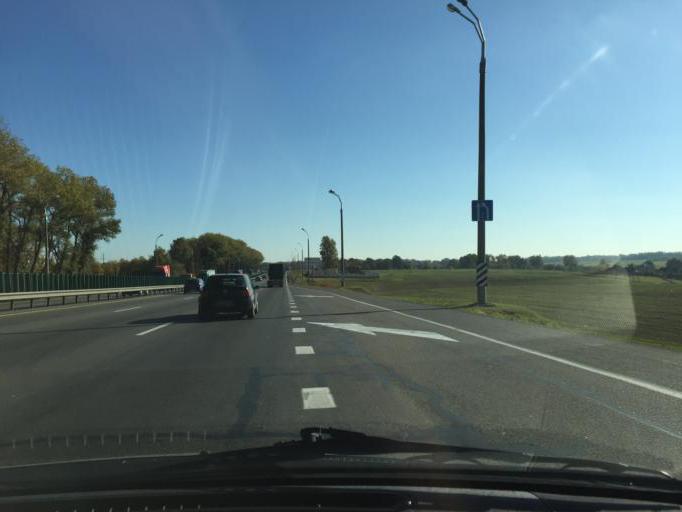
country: BY
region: Minsk
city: Syenitsa
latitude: 53.8344
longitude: 27.5406
